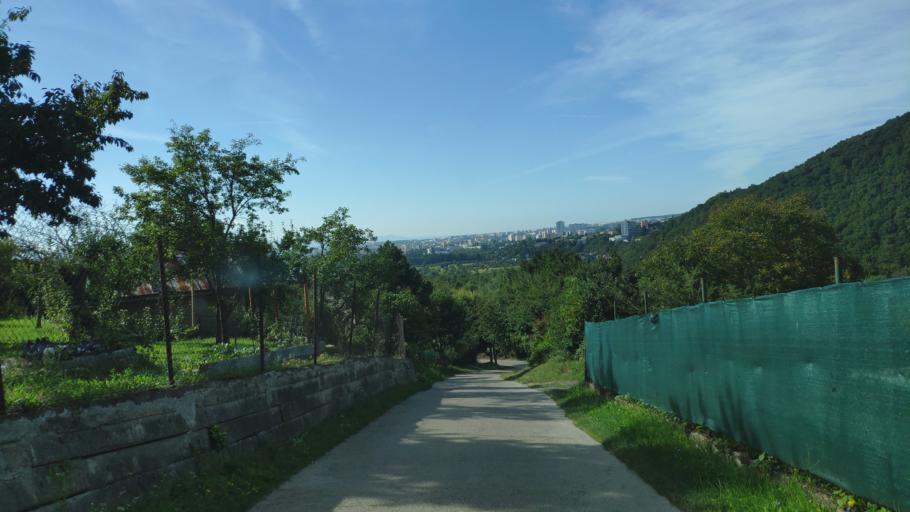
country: SK
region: Kosicky
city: Kosice
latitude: 48.7645
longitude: 21.2508
